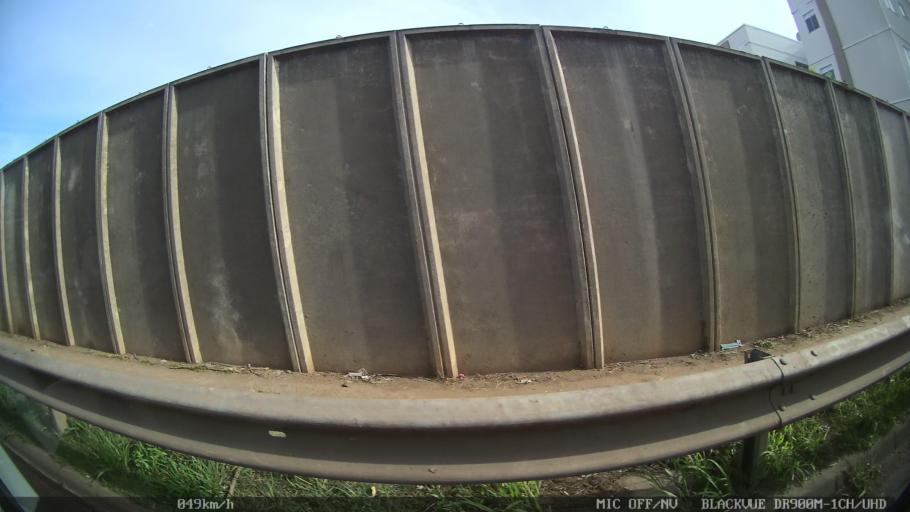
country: BR
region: Sao Paulo
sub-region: Piracicaba
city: Piracicaba
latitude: -22.6980
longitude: -47.6732
